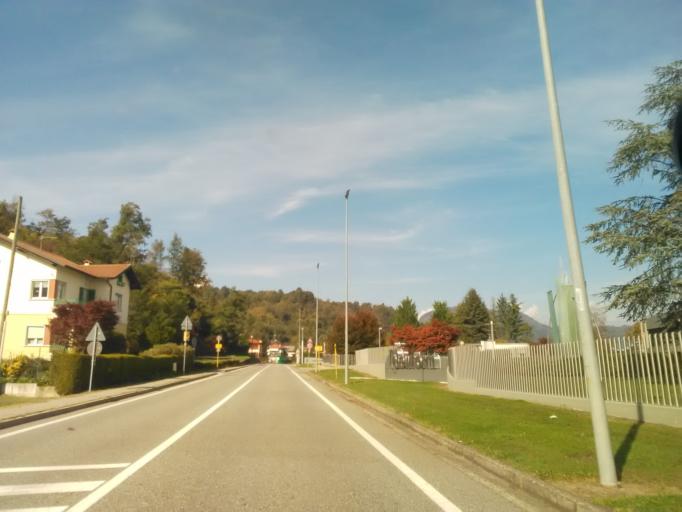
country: IT
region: Piedmont
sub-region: Provincia di Novara
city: Grignasco
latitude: 45.6598
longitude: 8.3346
